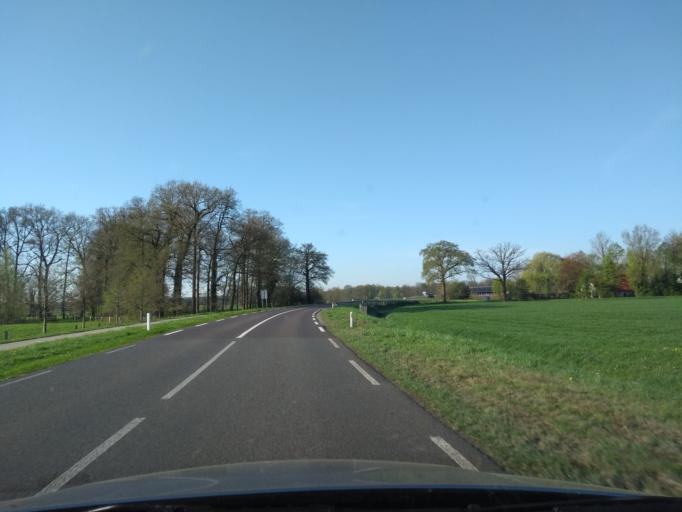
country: NL
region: Gelderland
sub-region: Berkelland
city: Neede
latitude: 52.1692
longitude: 6.6064
